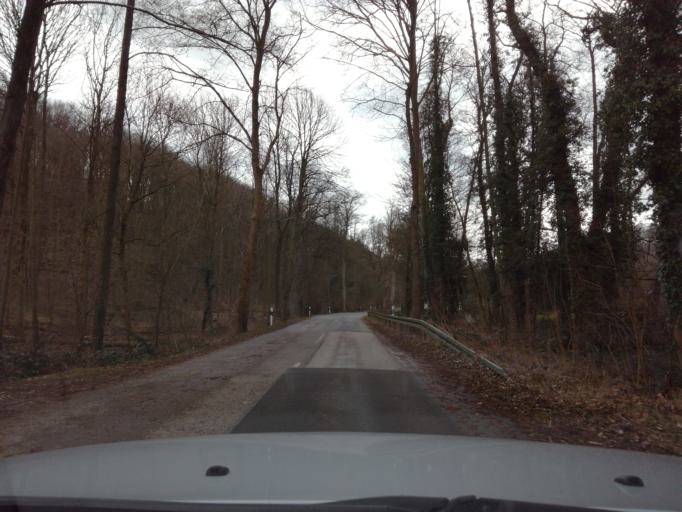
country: DE
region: North Rhine-Westphalia
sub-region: Regierungsbezirk Dusseldorf
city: Velbert
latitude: 51.3761
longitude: 7.0391
